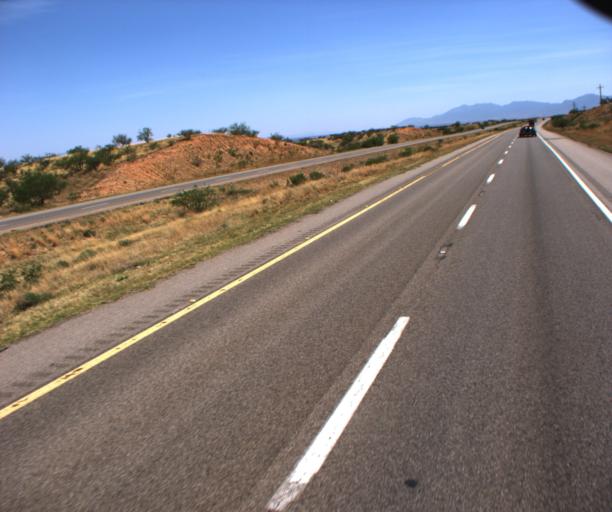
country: US
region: Arizona
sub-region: Cochise County
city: Whetstone
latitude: 31.8539
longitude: -110.3413
